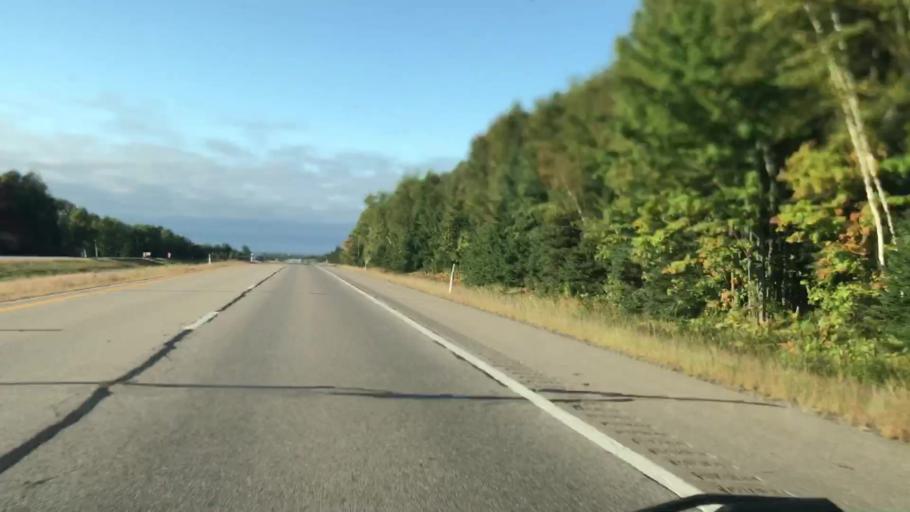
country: US
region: Michigan
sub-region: Chippewa County
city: Sault Ste. Marie
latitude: 46.4263
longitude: -84.3926
